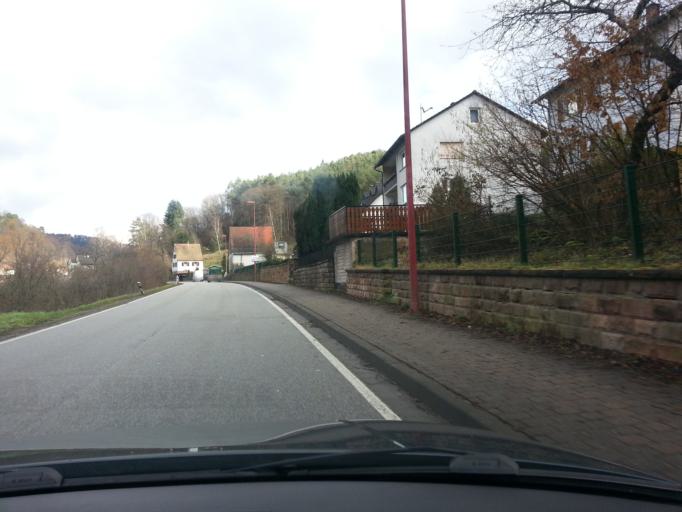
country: DE
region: Rheinland-Pfalz
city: Frankenstein
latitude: 49.4433
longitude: 7.9879
